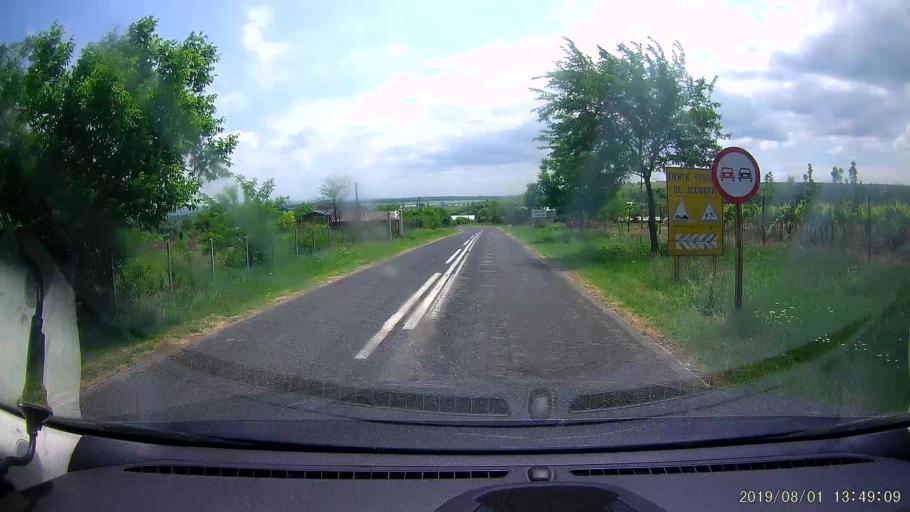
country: RO
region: Galati
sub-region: Comuna Oancea
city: Oancea
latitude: 45.8986
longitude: 28.1091
